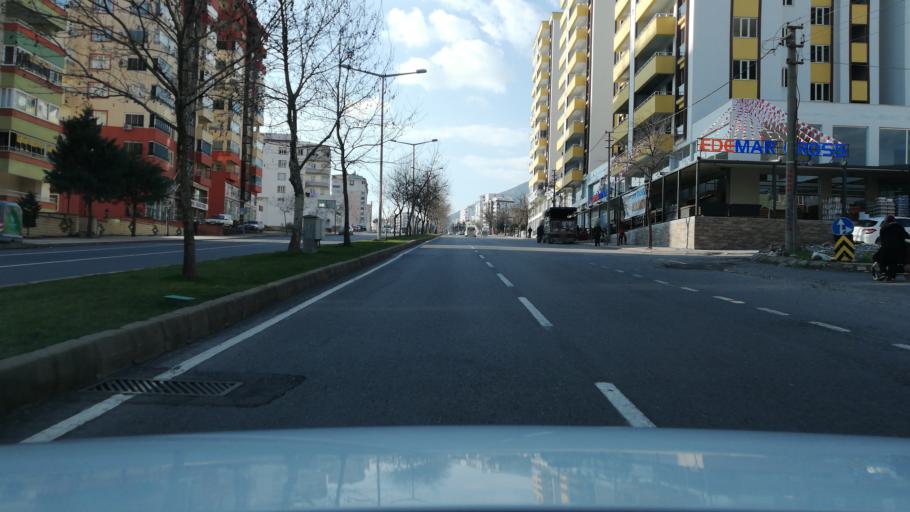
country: TR
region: Kahramanmaras
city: Kahramanmaras
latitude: 37.5940
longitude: 36.8950
